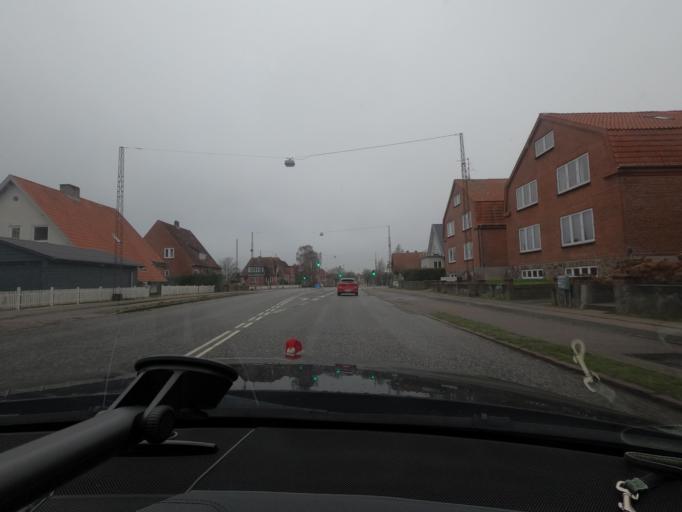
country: DK
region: South Denmark
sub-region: Sonderborg Kommune
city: Sonderborg
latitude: 54.9081
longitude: 9.8051
